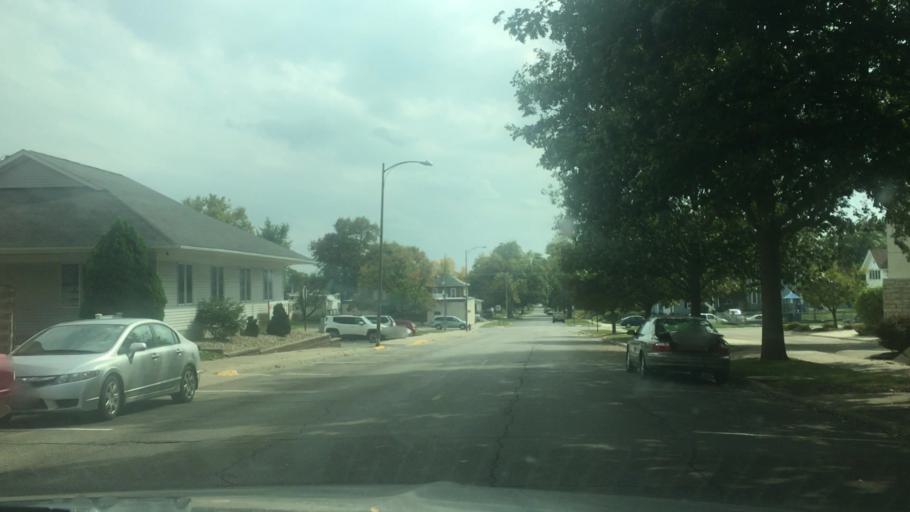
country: US
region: Iowa
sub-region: Marshall County
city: Marshalltown
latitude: 42.0489
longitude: -92.9163
